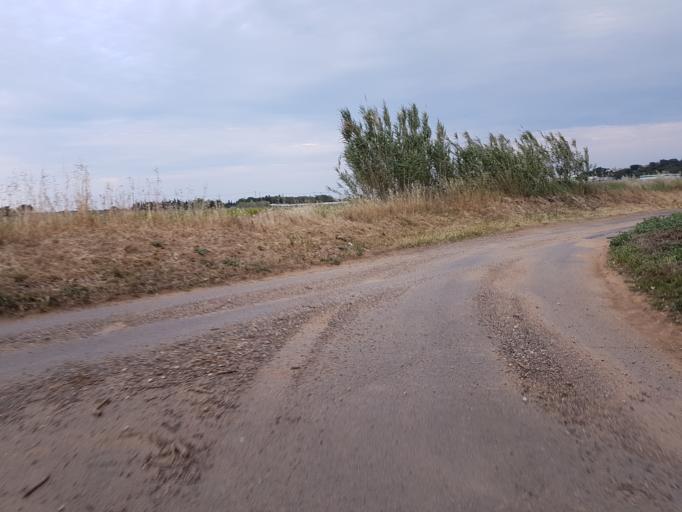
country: FR
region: Languedoc-Roussillon
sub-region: Departement de l'Herault
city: Portiragnes
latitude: 43.3159
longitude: 3.3354
